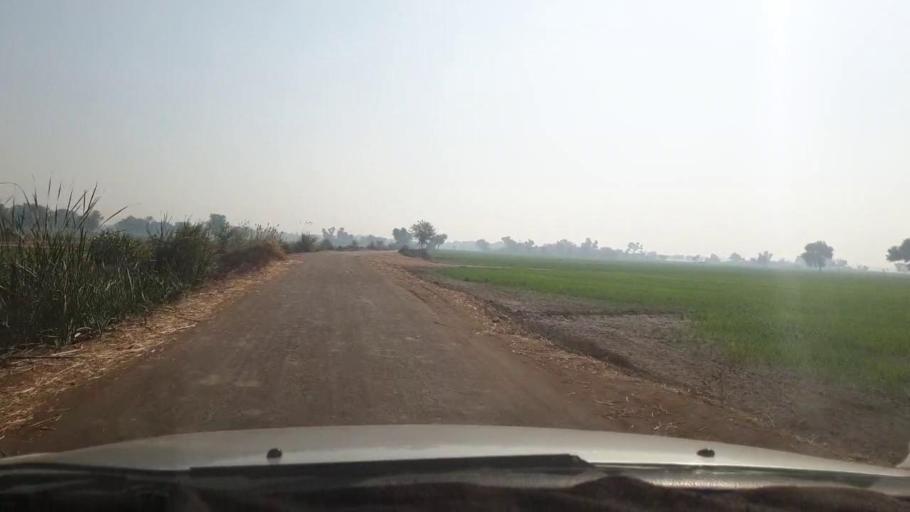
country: PK
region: Sindh
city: Khanpur
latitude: 27.7361
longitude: 69.5098
